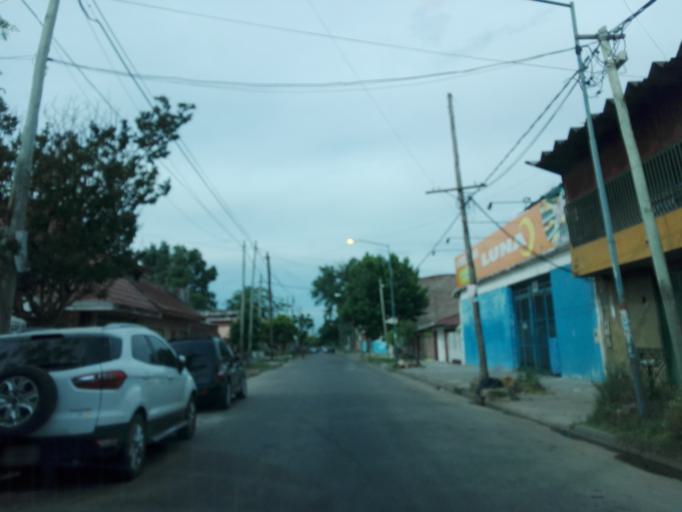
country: AR
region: Buenos Aires
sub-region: Partido de Lanus
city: Lanus
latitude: -34.7247
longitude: -58.3878
